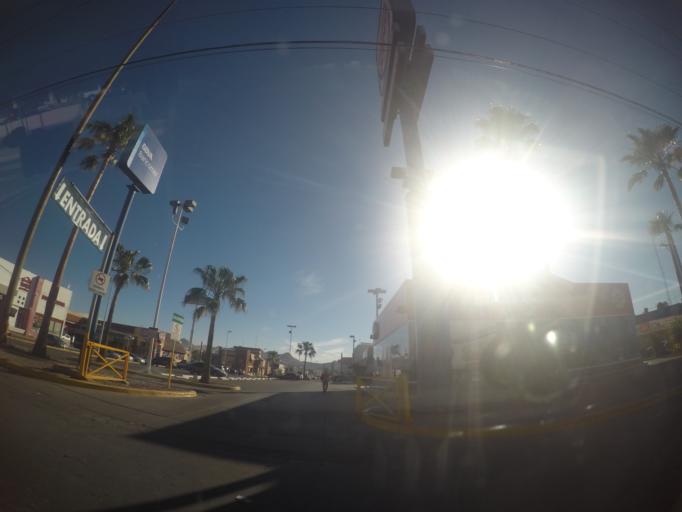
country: MX
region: Chihuahua
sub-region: Chihuahua
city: Chihuahua
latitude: 28.6720
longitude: -106.1017
